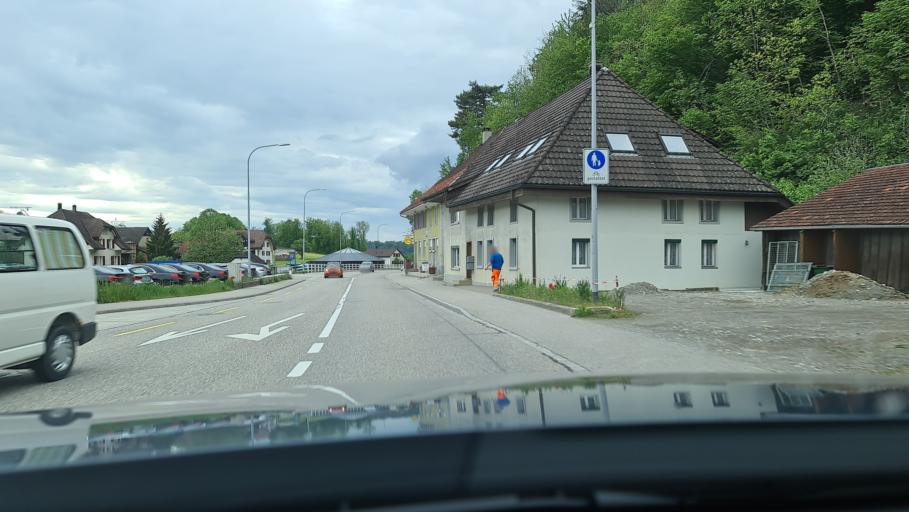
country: CH
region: Aargau
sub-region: Bezirk Zofingen
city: Kirchleerau
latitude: 47.2763
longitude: 8.0630
